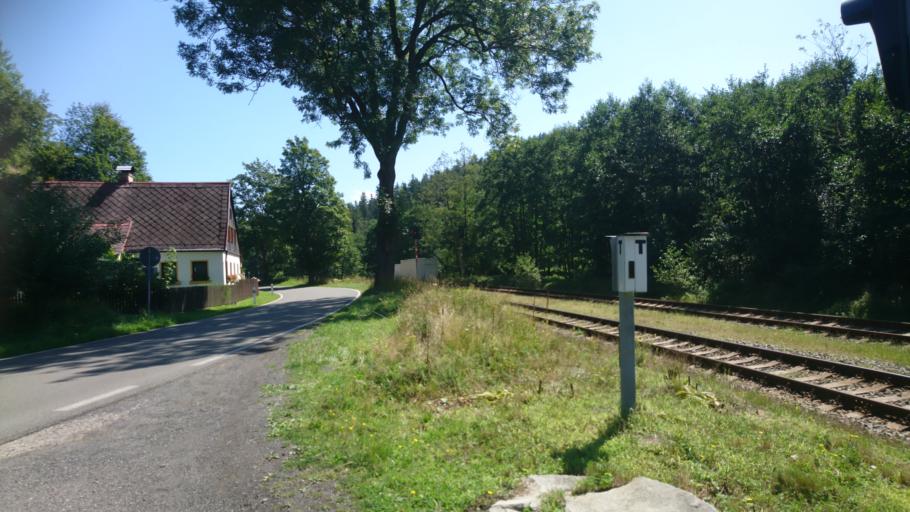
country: CZ
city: Kamenicky Senov
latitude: 50.8108
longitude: 14.4999
